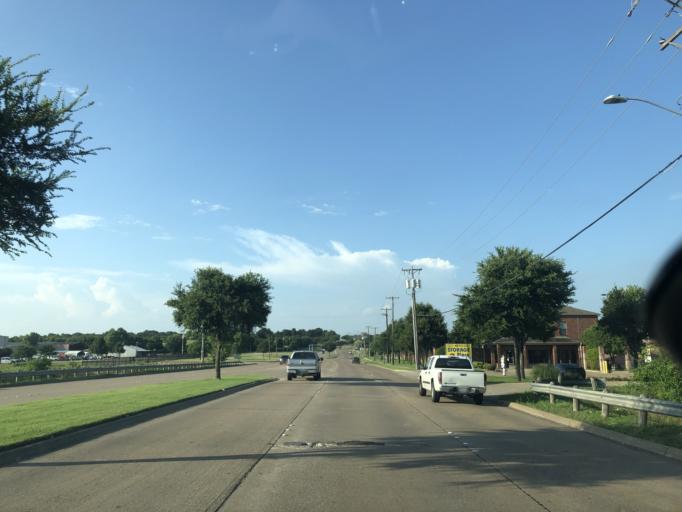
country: US
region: Texas
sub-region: Dallas County
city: Sunnyvale
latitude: 32.8319
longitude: -96.5958
